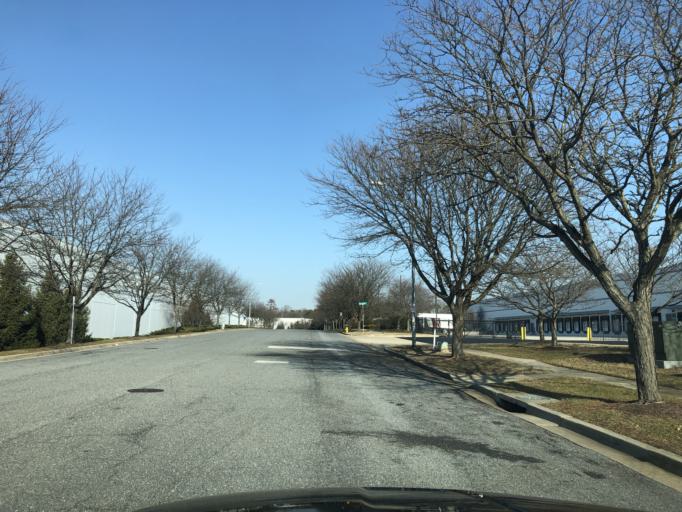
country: US
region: Maryland
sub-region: Anne Arundel County
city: Odenton
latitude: 39.0905
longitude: -76.6906
